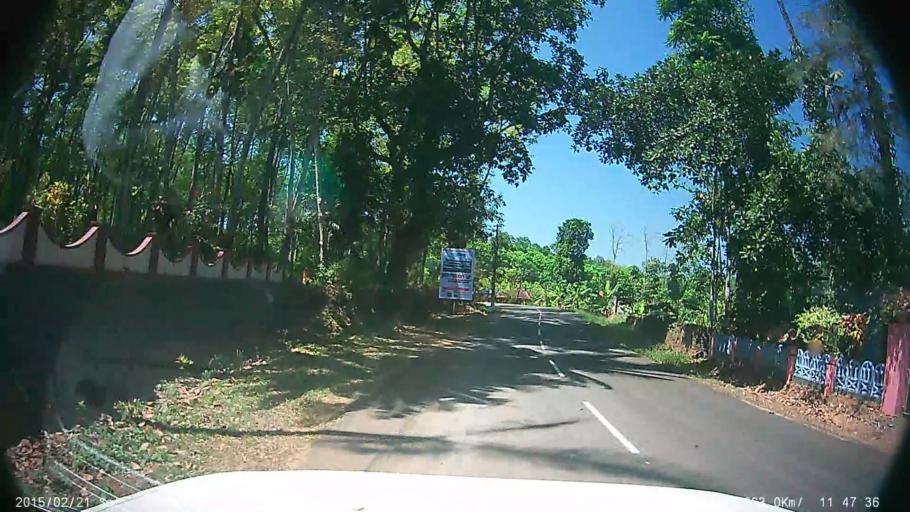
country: IN
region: Kerala
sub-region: Kottayam
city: Lalam
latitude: 9.7749
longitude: 76.7149
